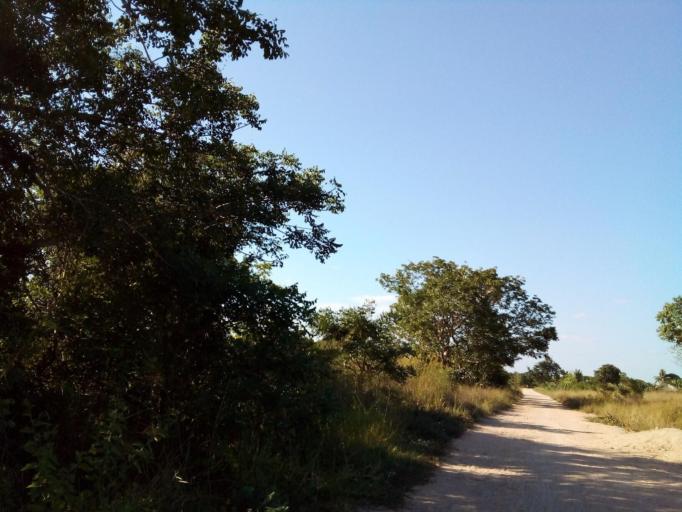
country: MZ
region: Zambezia
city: Quelimane
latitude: -17.5232
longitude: 36.6827
